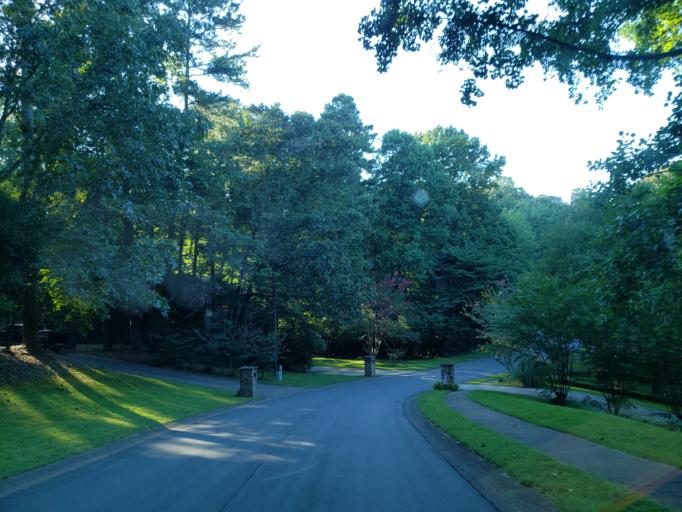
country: US
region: Georgia
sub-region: Fulton County
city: Roswell
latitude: 34.0109
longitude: -84.4499
